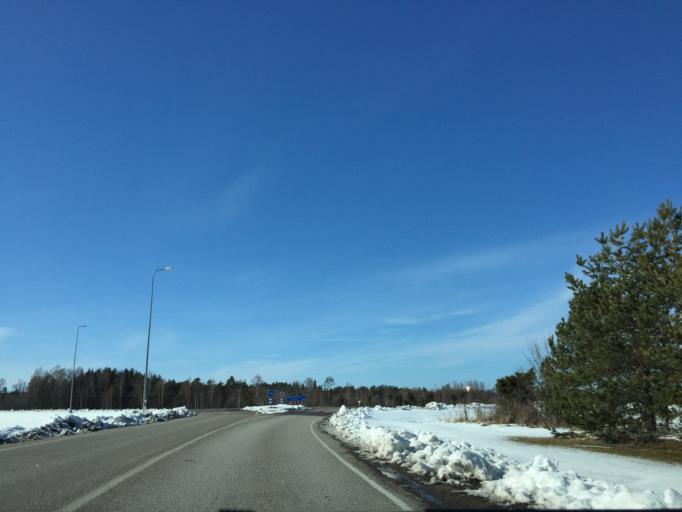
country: EE
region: Saare
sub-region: Kuressaare linn
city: Kuressaare
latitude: 58.3534
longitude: 22.7074
